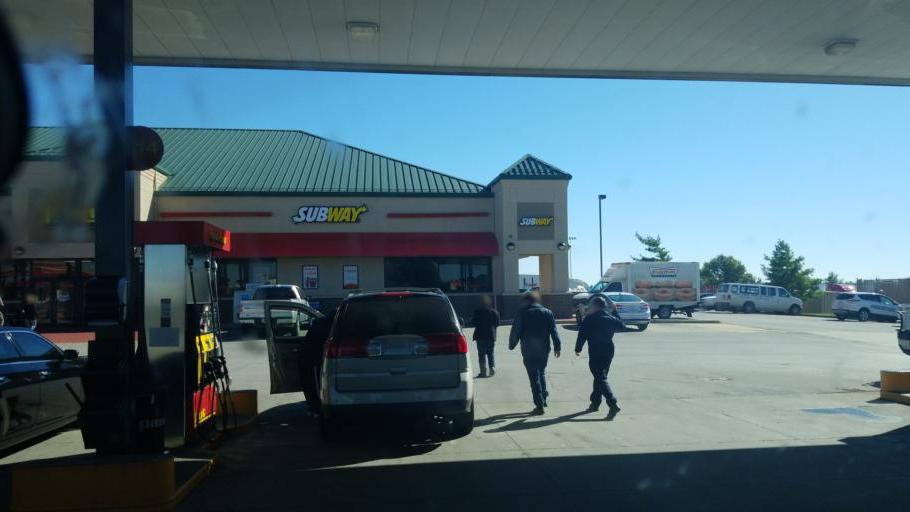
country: US
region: Missouri
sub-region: Lafayette County
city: Higginsville
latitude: 39.0031
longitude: -93.7348
